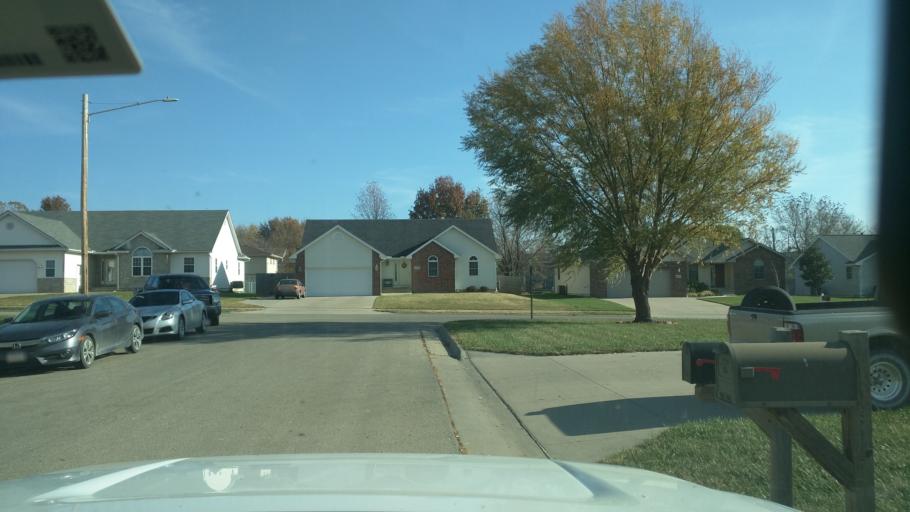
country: US
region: Kansas
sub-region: Lyon County
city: Emporia
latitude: 38.4229
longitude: -96.2299
